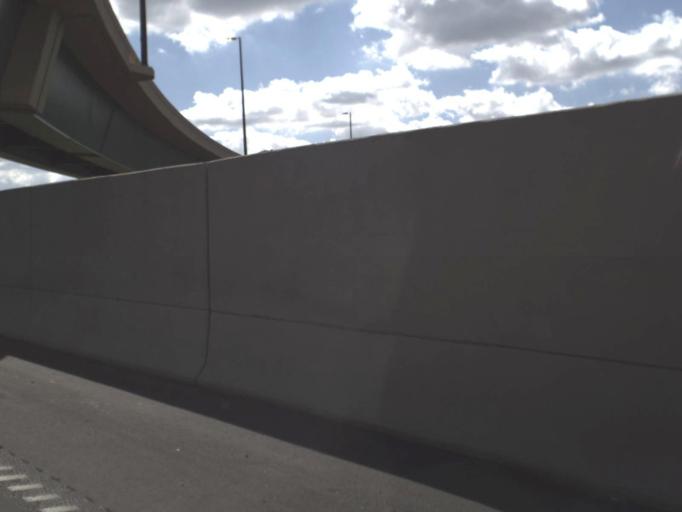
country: US
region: Florida
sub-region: Broward County
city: Broadview Park
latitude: 26.0936
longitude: -80.2171
